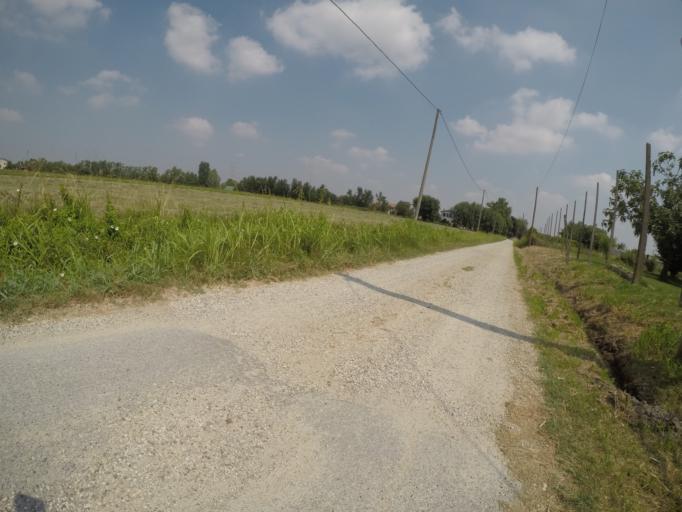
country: IT
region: Veneto
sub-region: Provincia di Rovigo
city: Villanova del Ghebbo Canton
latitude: 45.0620
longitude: 11.6403
